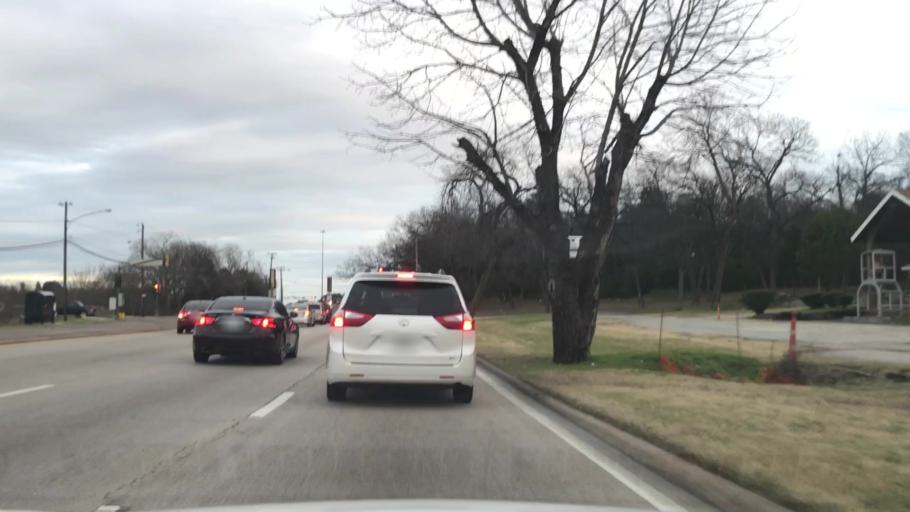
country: US
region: Texas
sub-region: Dallas County
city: Cockrell Hill
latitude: 32.6891
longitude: -96.8296
